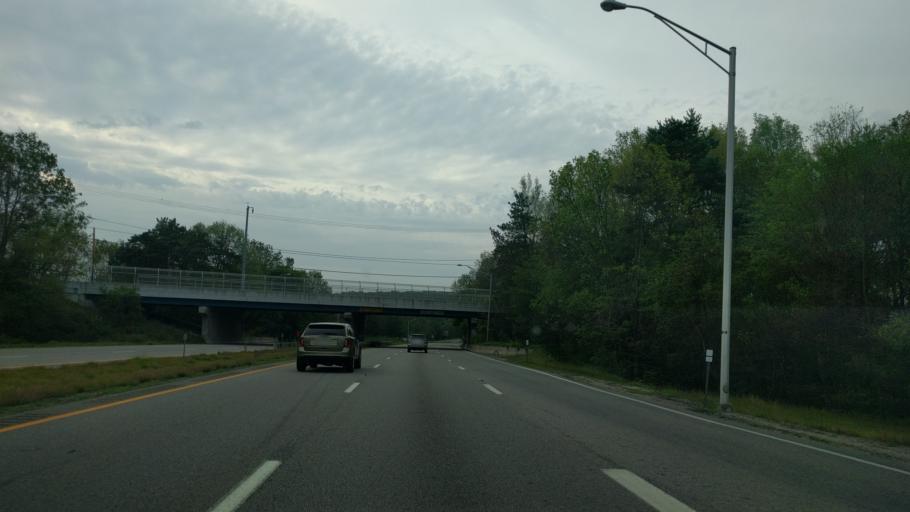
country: US
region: Massachusetts
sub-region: Worcester County
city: Blackstone
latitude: 42.0010
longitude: -71.5597
